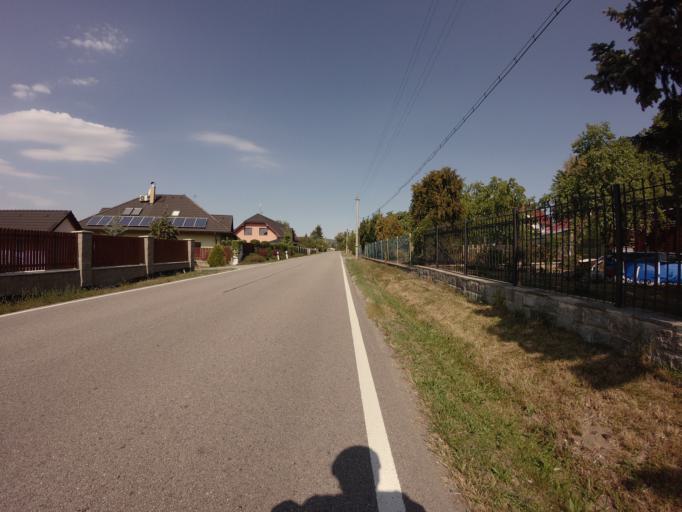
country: CZ
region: Central Bohemia
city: Kamenny Privoz
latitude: 49.8604
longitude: 14.5138
